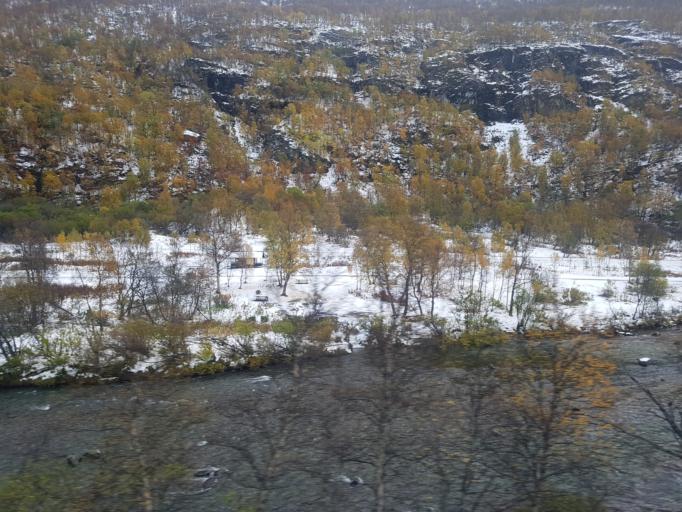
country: NO
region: Sor-Trondelag
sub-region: Oppdal
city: Oppdal
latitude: 62.4015
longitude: 9.6334
